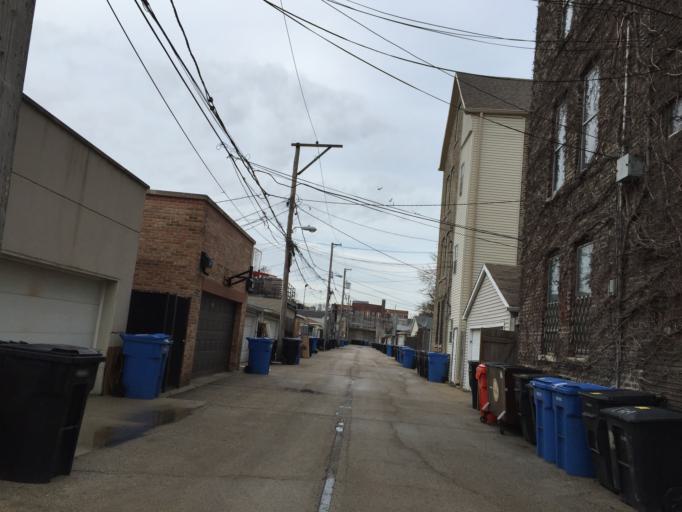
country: US
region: Illinois
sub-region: Cook County
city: Chicago
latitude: 41.9128
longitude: -87.6745
